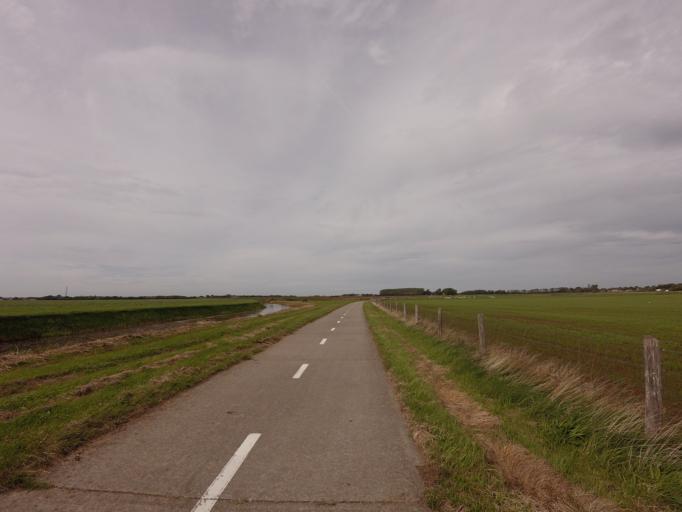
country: NL
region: North Holland
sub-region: Gemeente Texel
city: Den Burg
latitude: 53.0612
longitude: 4.8260
